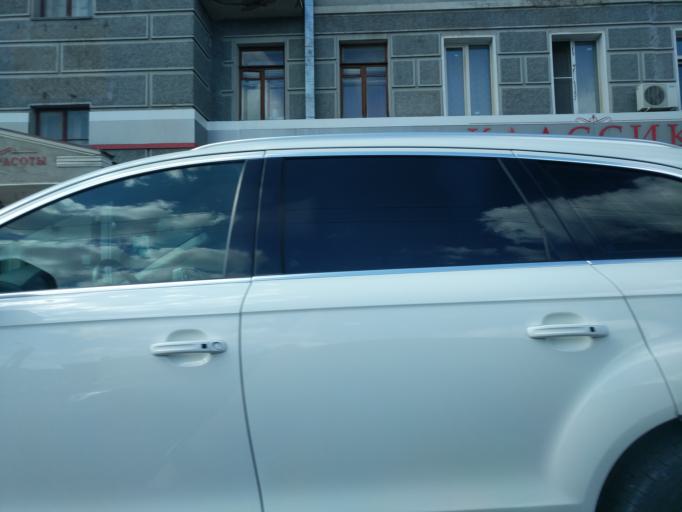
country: RU
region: Kirov
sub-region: Kirovo-Chepetskiy Rayon
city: Kirov
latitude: 58.6014
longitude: 49.6807
